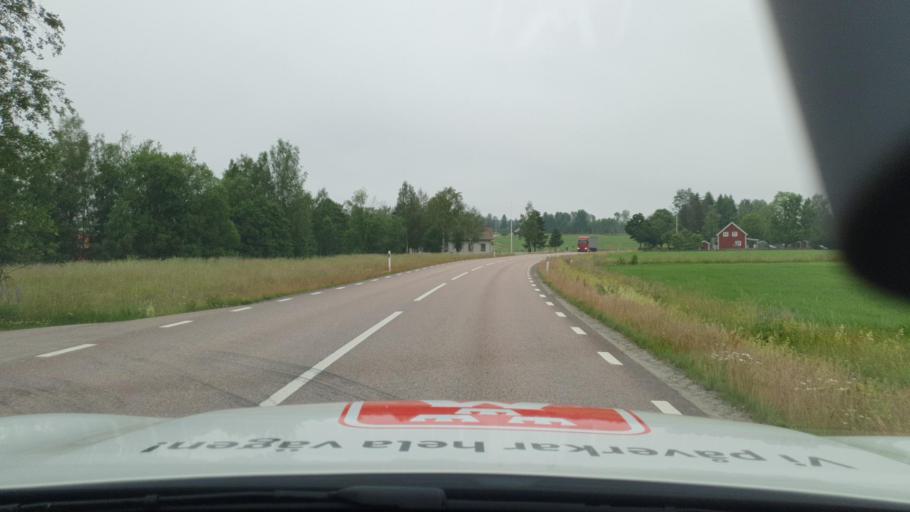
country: SE
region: Vaermland
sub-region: Sunne Kommun
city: Sunne
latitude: 59.6880
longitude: 13.1387
